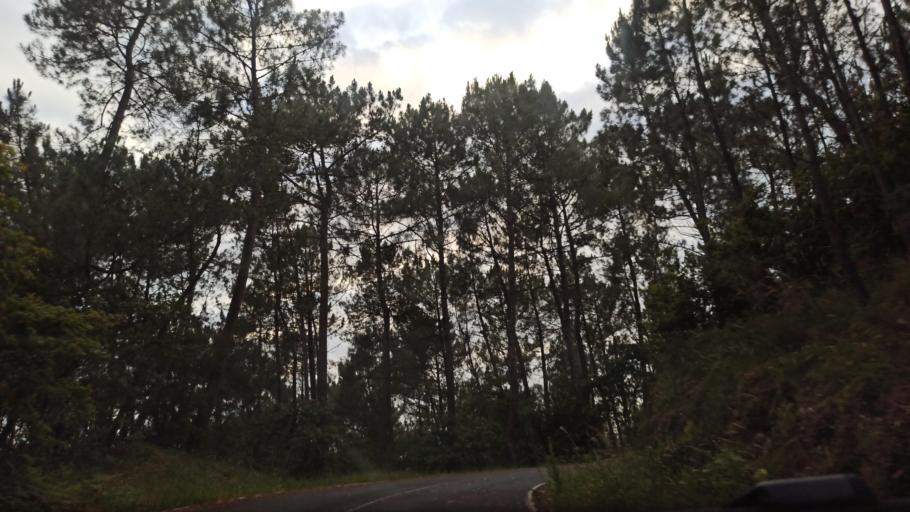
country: ES
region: Galicia
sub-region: Provincia da Coruna
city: Santiso
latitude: 42.8269
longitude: -8.1289
